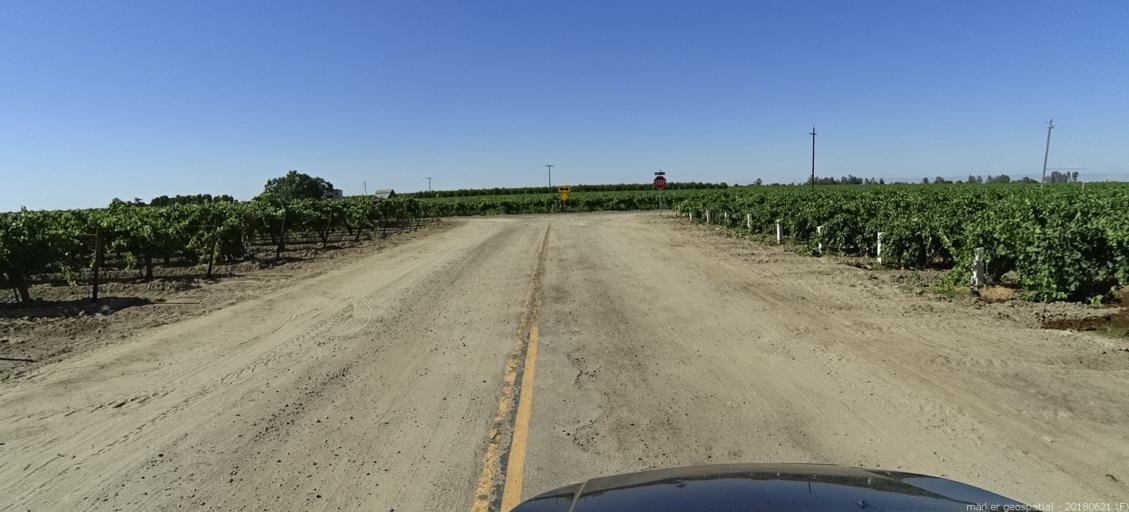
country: US
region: California
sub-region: Fresno County
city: Biola
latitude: 36.8373
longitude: -120.0463
